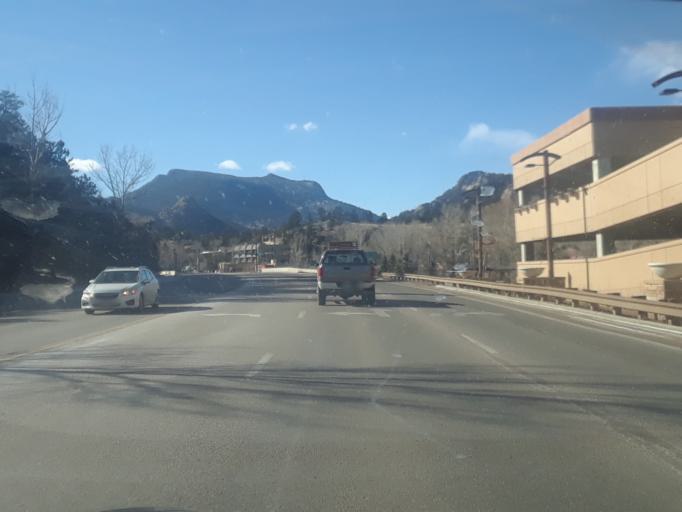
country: US
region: Colorado
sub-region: Larimer County
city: Estes Park
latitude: 40.3776
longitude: -105.5136
